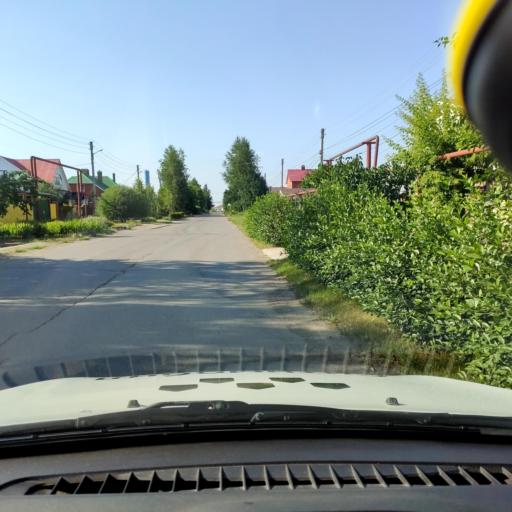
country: RU
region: Samara
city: Podstepki
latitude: 53.5187
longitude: 49.1808
